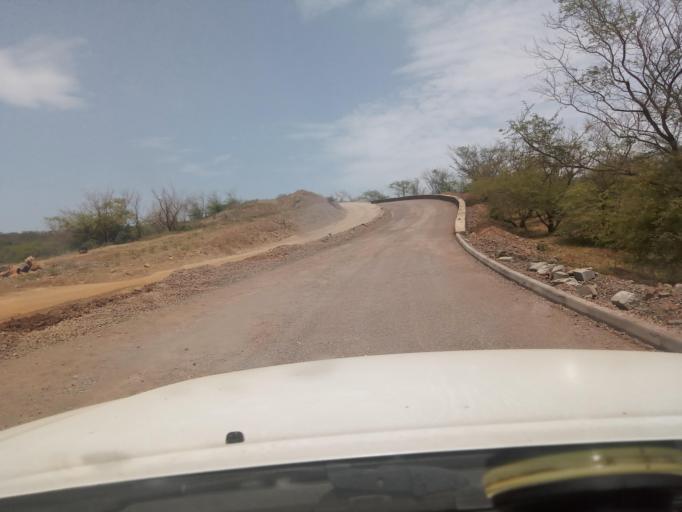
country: CV
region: Ribeira Grande de Santiago
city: Cidade Velha
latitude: 14.9805
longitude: -23.6141
